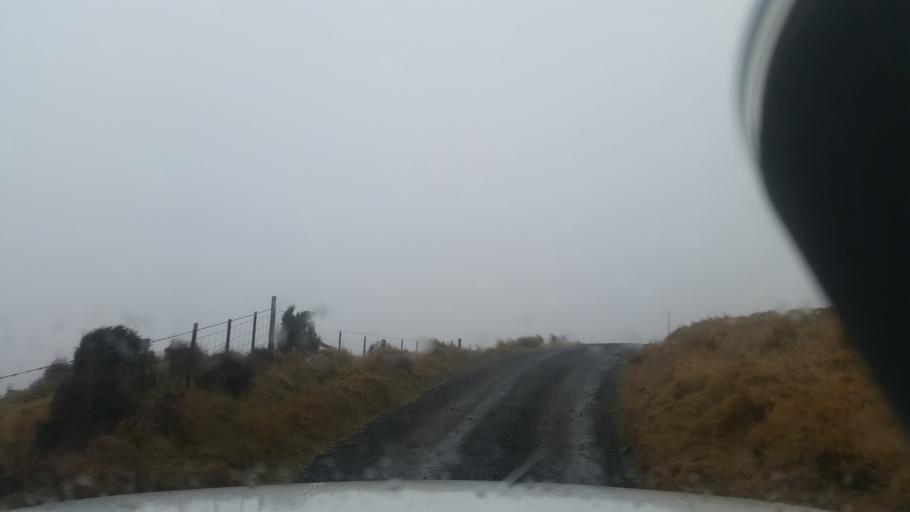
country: NZ
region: Canterbury
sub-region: Christchurch City
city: Christchurch
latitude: -43.8594
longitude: 172.8917
